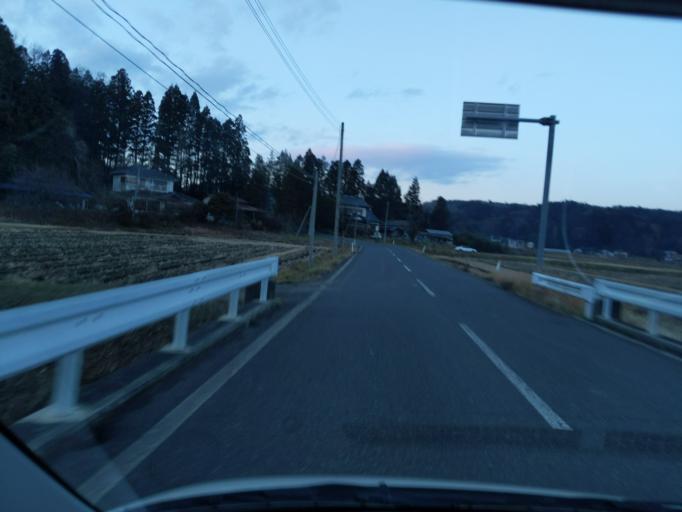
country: JP
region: Iwate
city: Ichinoseki
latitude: 38.8375
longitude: 141.1291
